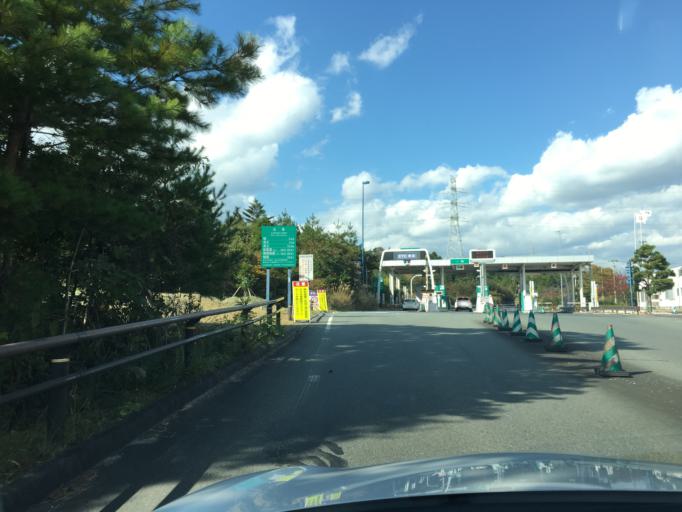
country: JP
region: Fukushima
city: Iwaki
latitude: 37.2351
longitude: 140.9857
